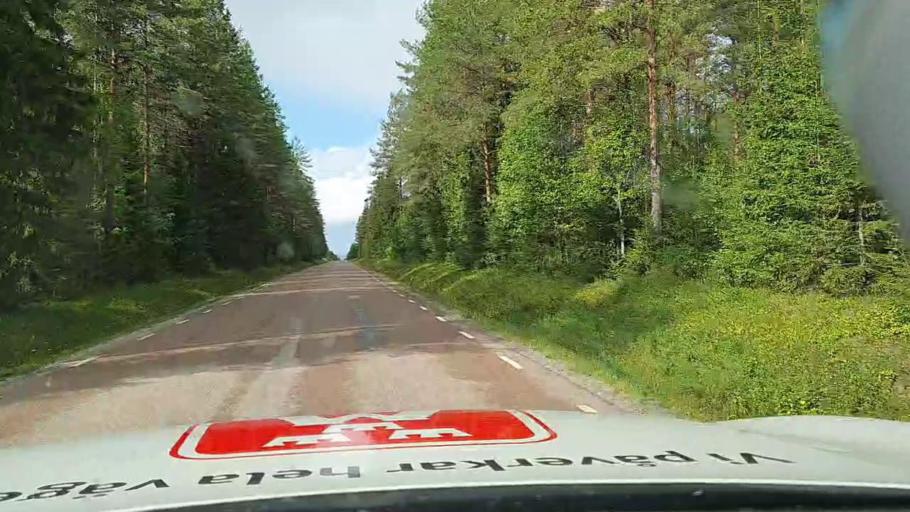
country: SE
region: Jaemtland
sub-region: Stroemsunds Kommun
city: Stroemsund
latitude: 63.8682
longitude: 15.3745
